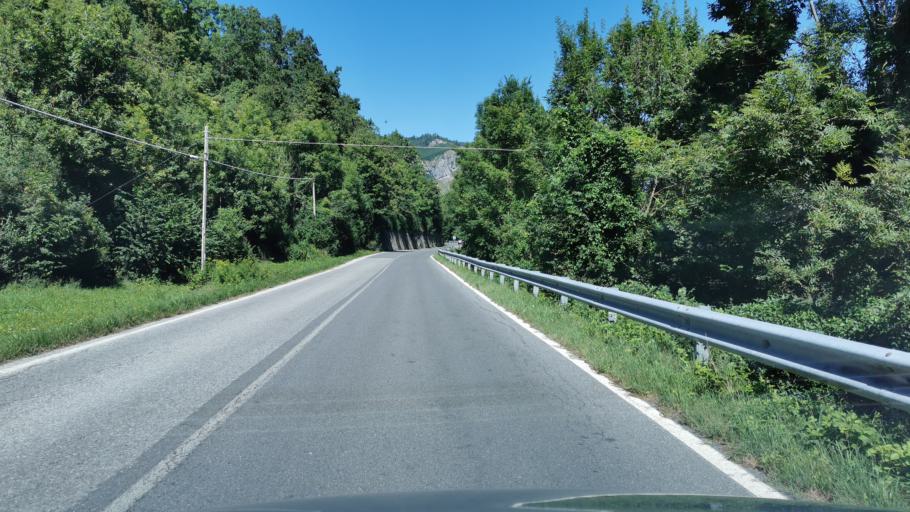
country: IT
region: Piedmont
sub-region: Provincia di Cuneo
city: Valdieri
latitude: 44.2871
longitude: 7.4183
